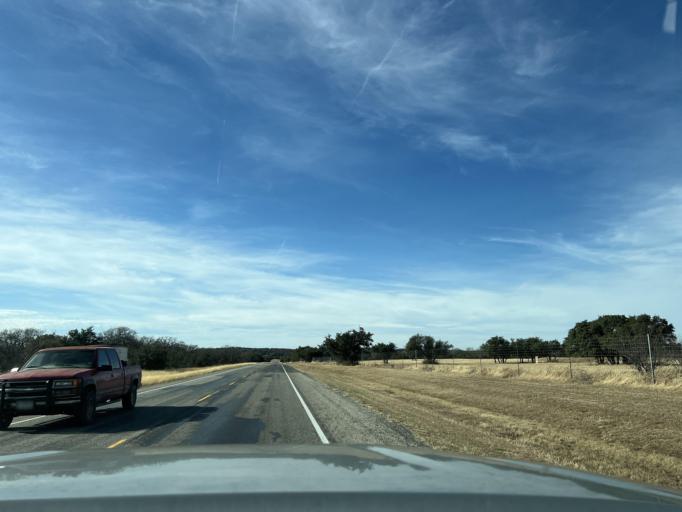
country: US
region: Texas
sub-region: Eastland County
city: Cisco
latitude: 32.4599
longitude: -99.0001
